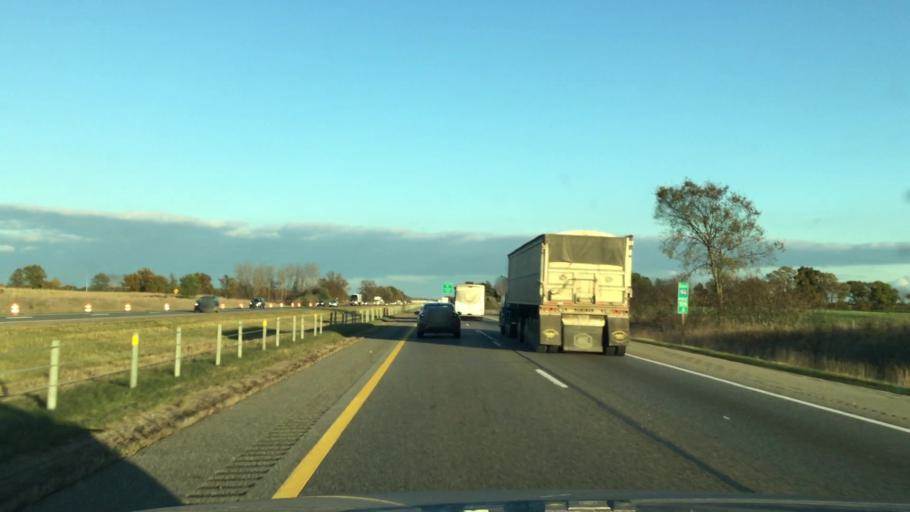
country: US
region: Michigan
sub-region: Calhoun County
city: Marshall
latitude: 42.2985
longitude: -85.0297
